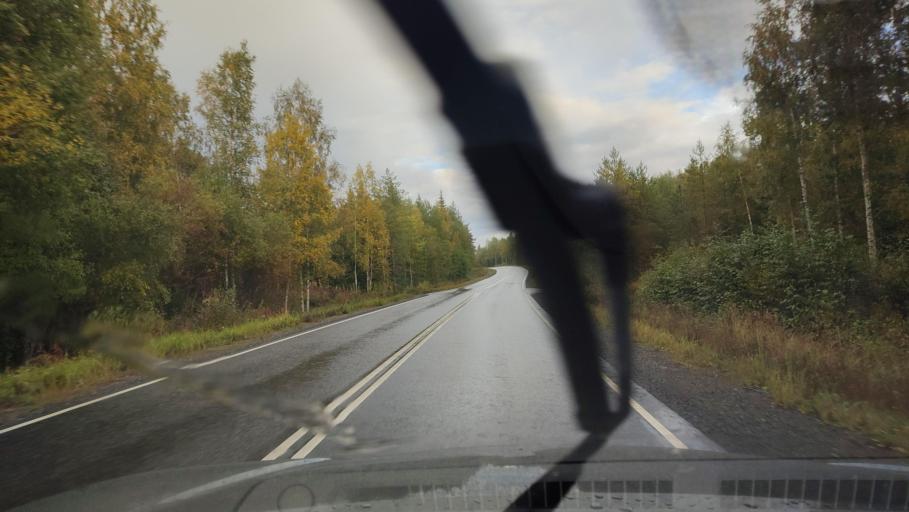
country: FI
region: Southern Ostrobothnia
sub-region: Suupohja
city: Karijoki
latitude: 62.2764
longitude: 21.5756
